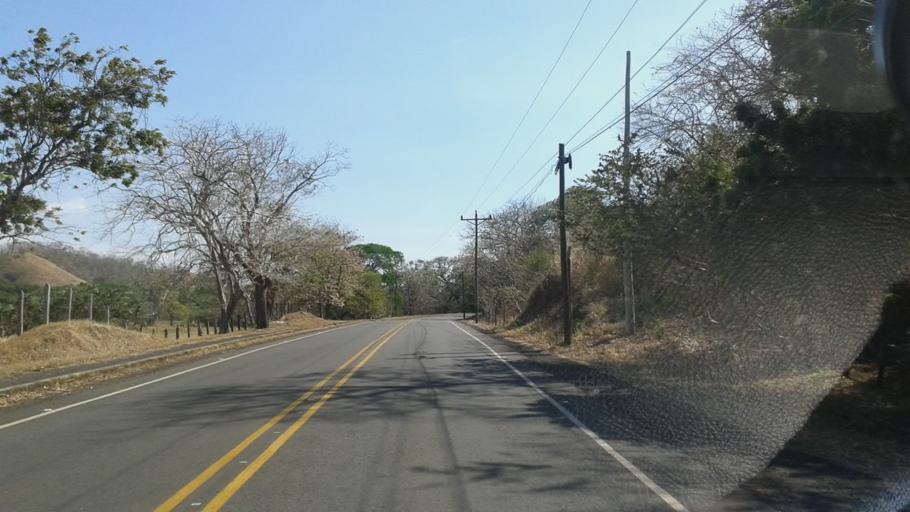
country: CR
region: Guanacaste
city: Santa Cruz
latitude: 10.2244
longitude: -85.7494
